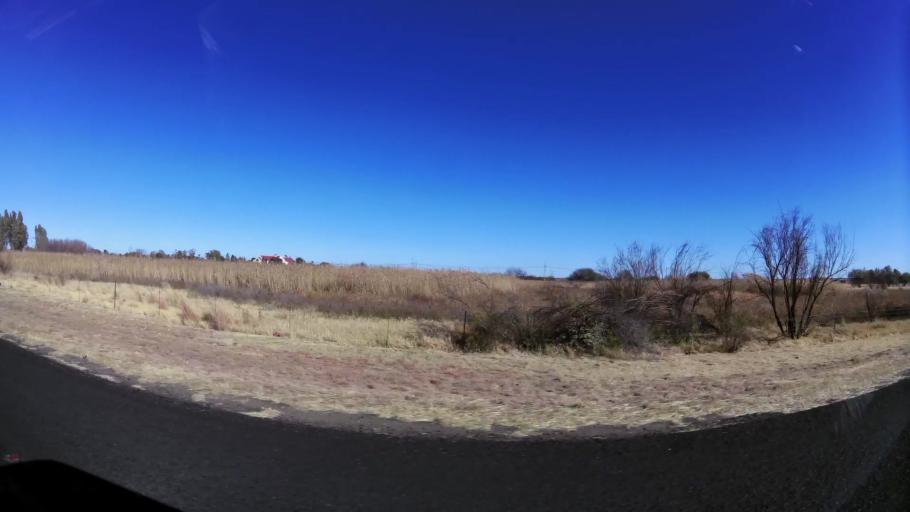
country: ZA
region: Northern Cape
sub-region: Frances Baard District Municipality
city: Kimberley
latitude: -28.6868
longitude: 24.7784
